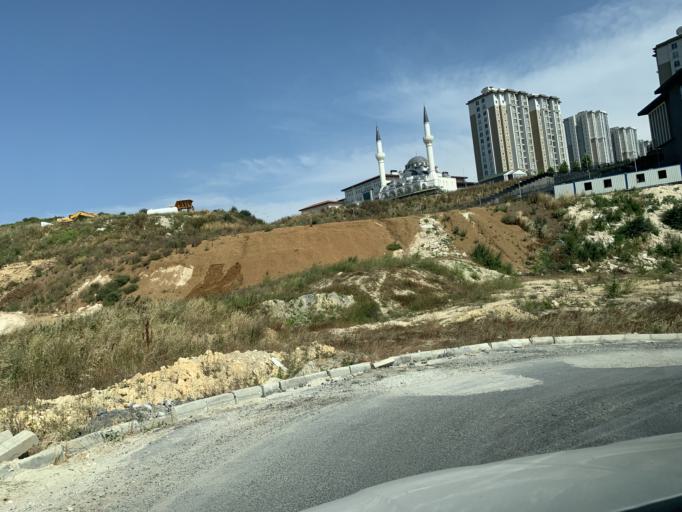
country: TR
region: Istanbul
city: Esenyurt
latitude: 41.0833
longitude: 28.6901
